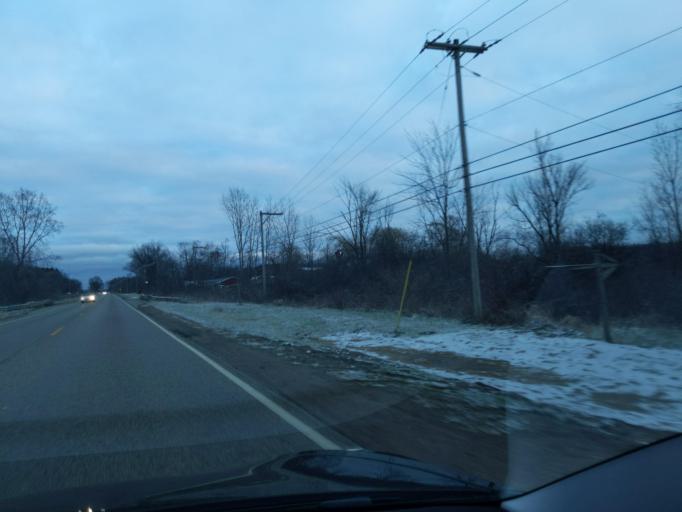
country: US
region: Michigan
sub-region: Jackson County
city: Spring Arbor
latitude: 42.2535
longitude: -84.5051
